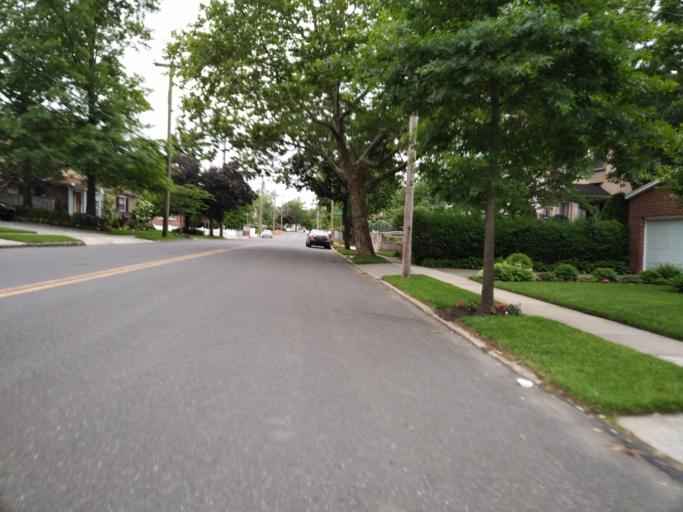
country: US
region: New York
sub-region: Nassau County
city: East Atlantic Beach
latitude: 40.7765
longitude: -73.7775
